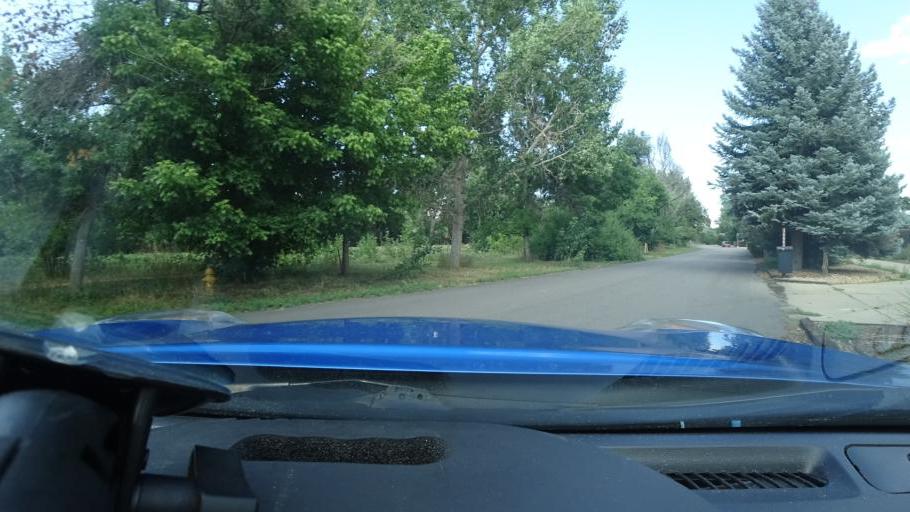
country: US
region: Colorado
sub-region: Adams County
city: Aurora
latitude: 39.7004
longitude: -104.8719
